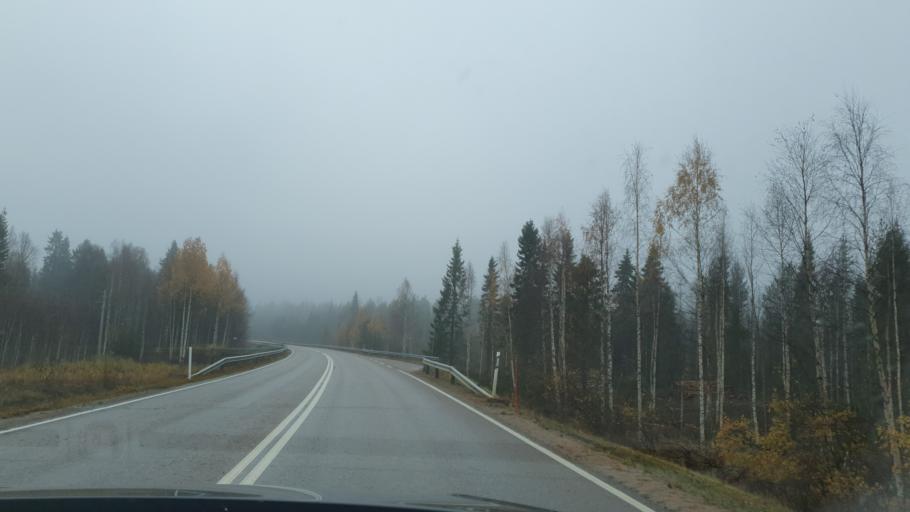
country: FI
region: Lapland
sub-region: Rovaniemi
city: Rovaniemi
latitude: 66.8165
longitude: 25.3958
